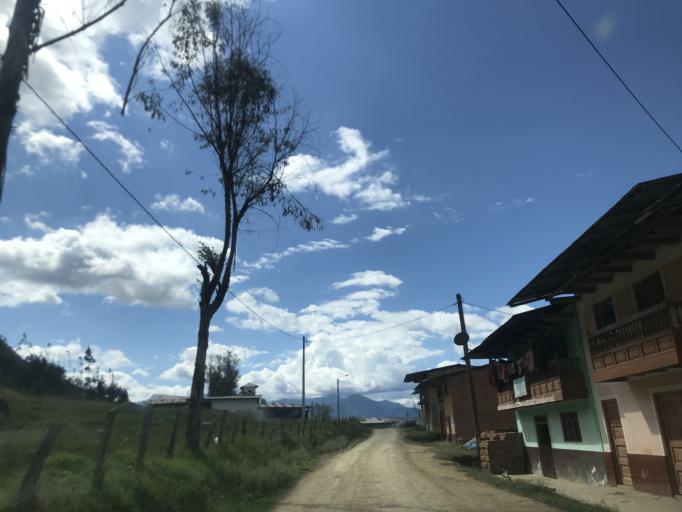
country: PE
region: Cajamarca
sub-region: Provincia de Chota
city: Querocoto
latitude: -6.3352
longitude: -79.0683
